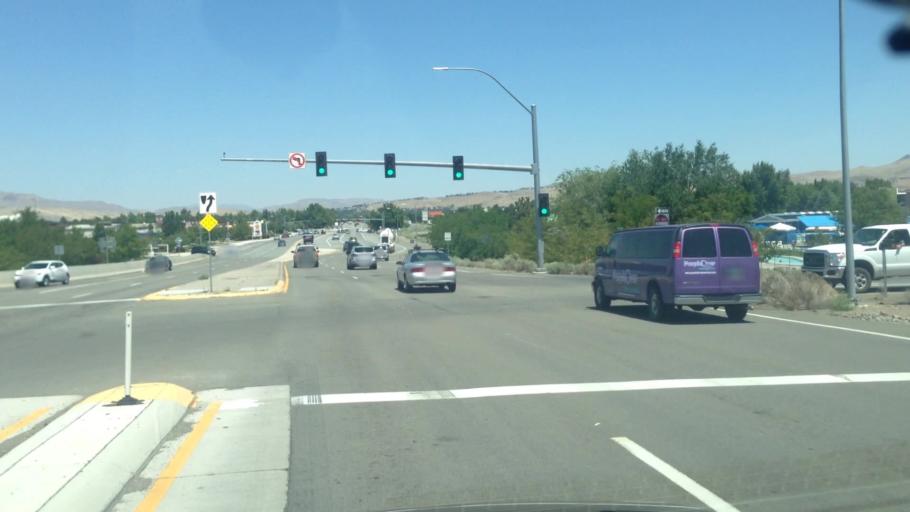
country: US
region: Nevada
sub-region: Washoe County
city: Sparks
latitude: 39.5296
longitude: -119.7152
